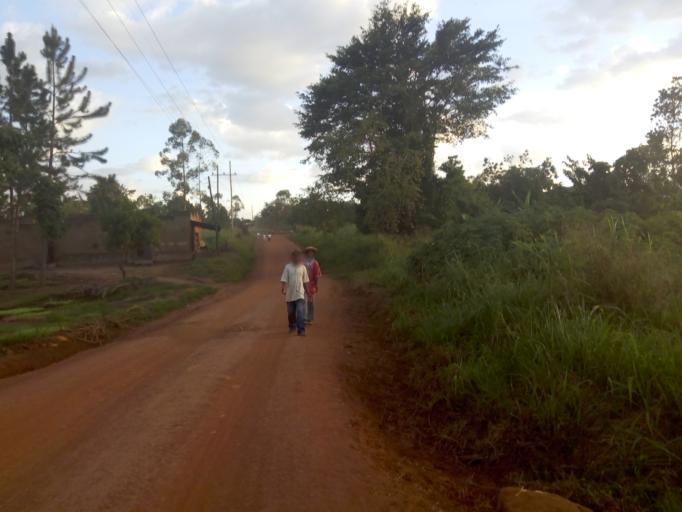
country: UG
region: Western Region
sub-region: Masindi District
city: Masindi
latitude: 1.6773
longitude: 31.7185
